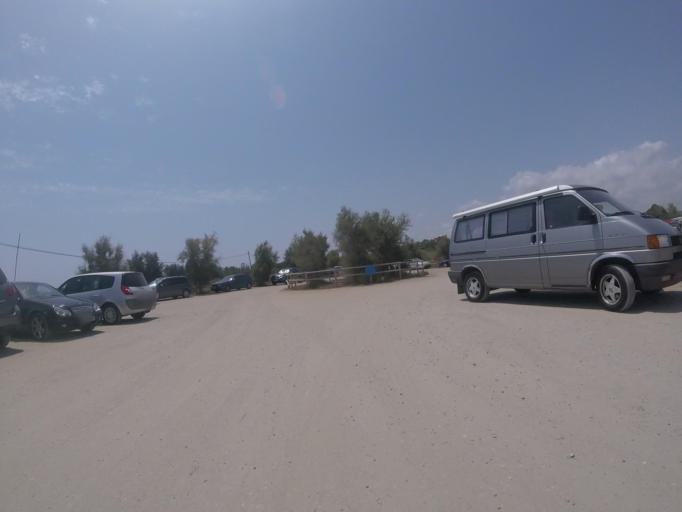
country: ES
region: Valencia
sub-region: Provincia de Castello
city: Orpesa/Oropesa del Mar
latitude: 40.1334
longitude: 0.1647
